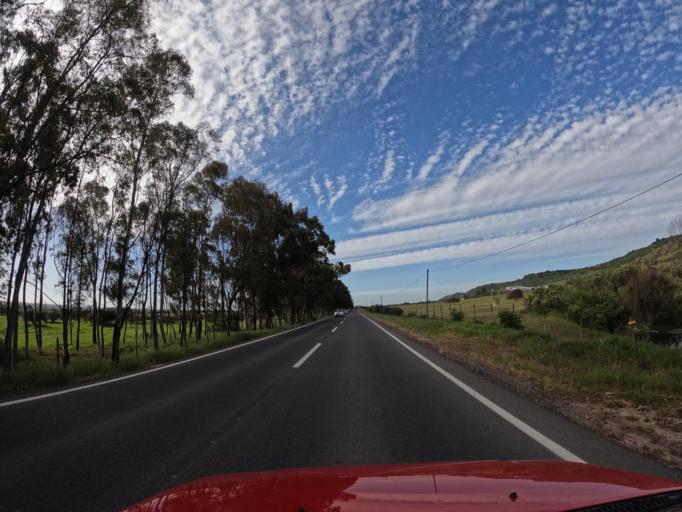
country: CL
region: O'Higgins
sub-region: Provincia de Colchagua
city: Santa Cruz
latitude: -34.1865
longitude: -71.7337
